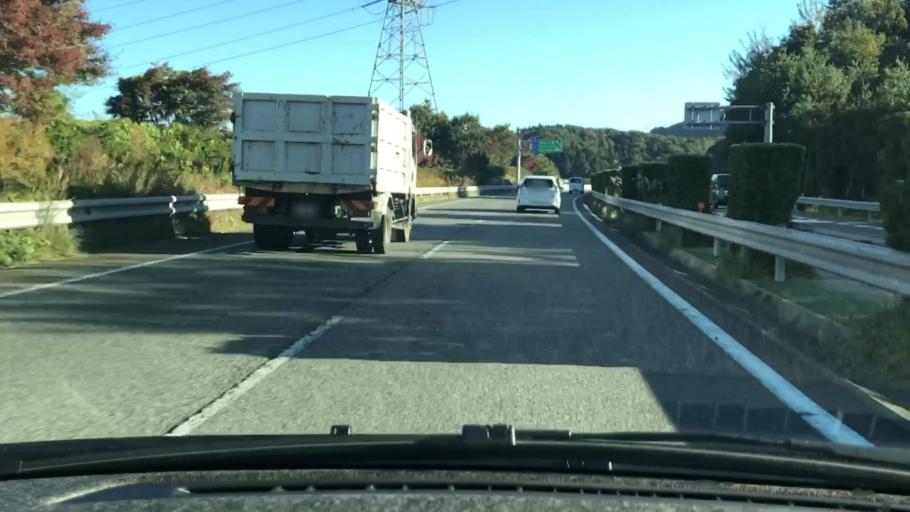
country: JP
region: Hyogo
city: Kobe
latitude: 34.7670
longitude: 135.1977
